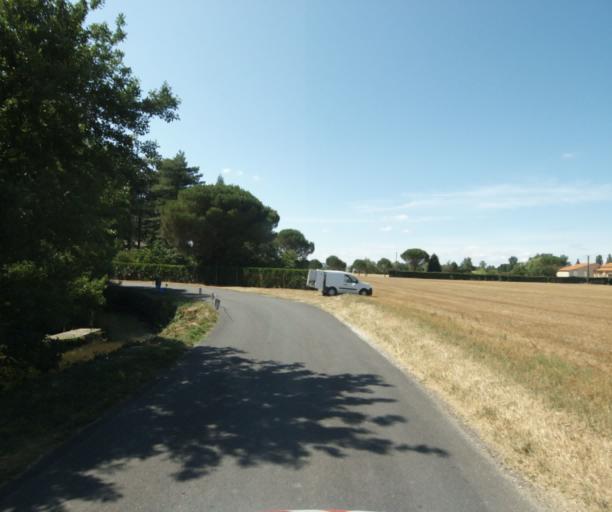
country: FR
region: Midi-Pyrenees
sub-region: Departement de la Haute-Garonne
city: Revel
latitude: 43.4749
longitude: 1.9941
